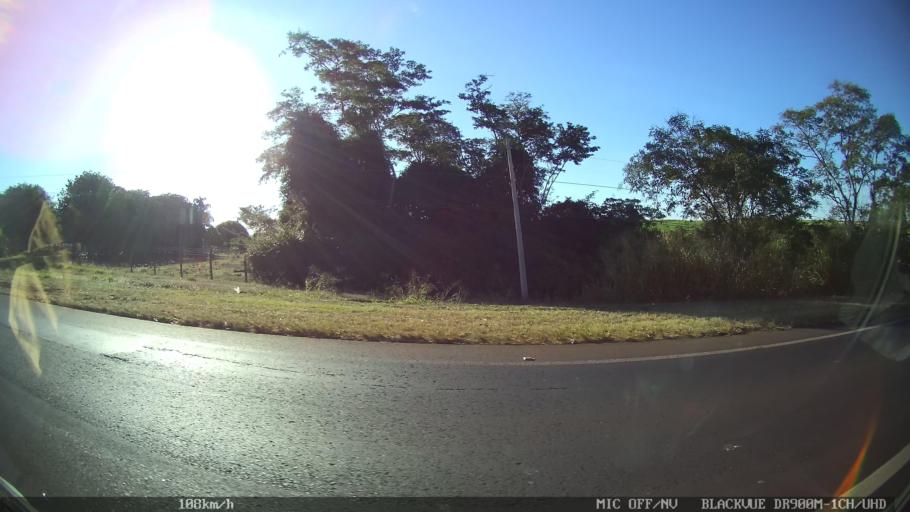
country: BR
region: Sao Paulo
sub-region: Olimpia
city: Olimpia
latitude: -20.7117
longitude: -48.9799
